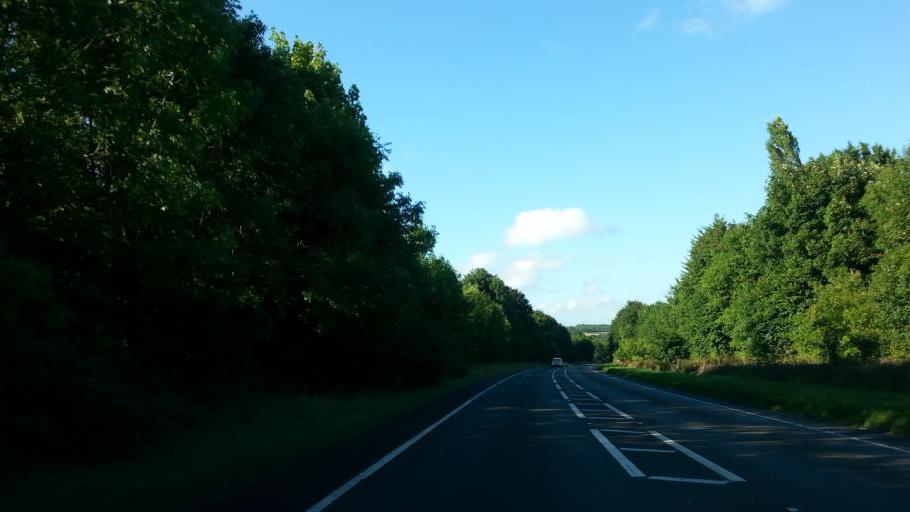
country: GB
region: England
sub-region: District of Rutland
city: Ketton
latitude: 52.5969
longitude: -0.5371
